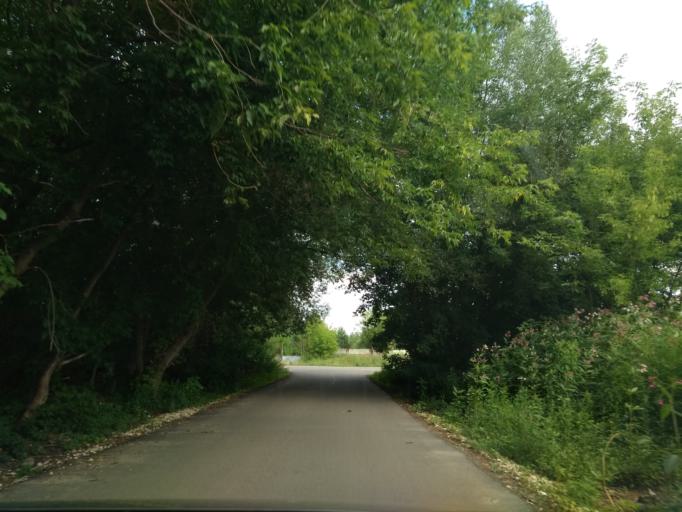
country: RU
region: Moskovskaya
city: Kabanovo
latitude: 55.7846
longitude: 38.9254
